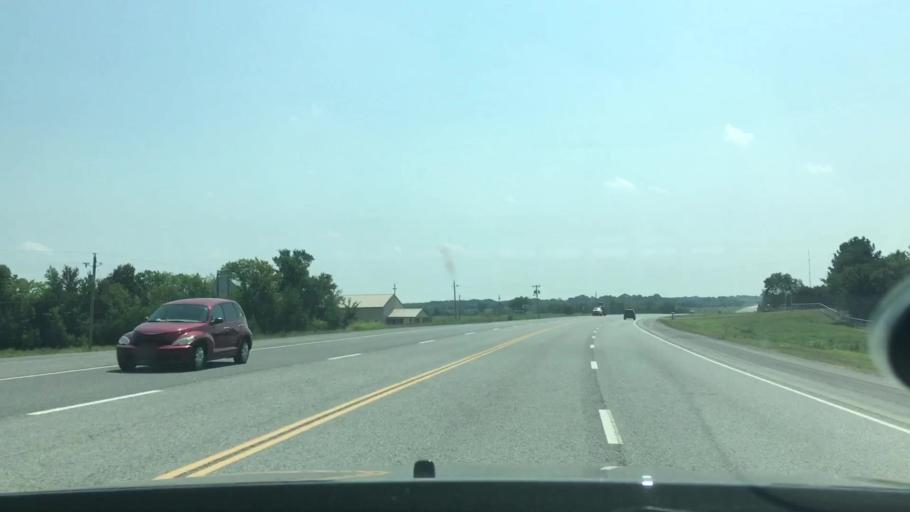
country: US
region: Oklahoma
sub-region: Atoka County
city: Atoka
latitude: 34.3716
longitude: -96.1078
